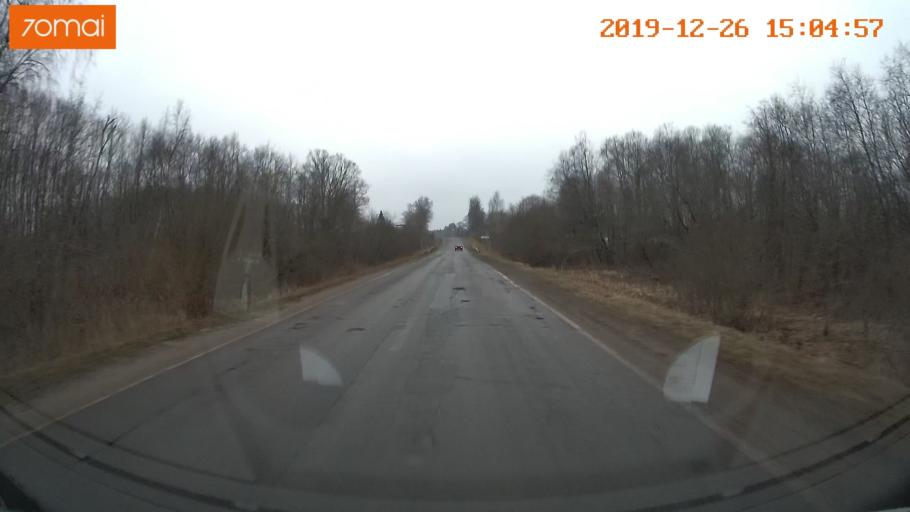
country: RU
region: Jaroslavl
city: Rybinsk
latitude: 58.1944
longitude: 38.8565
